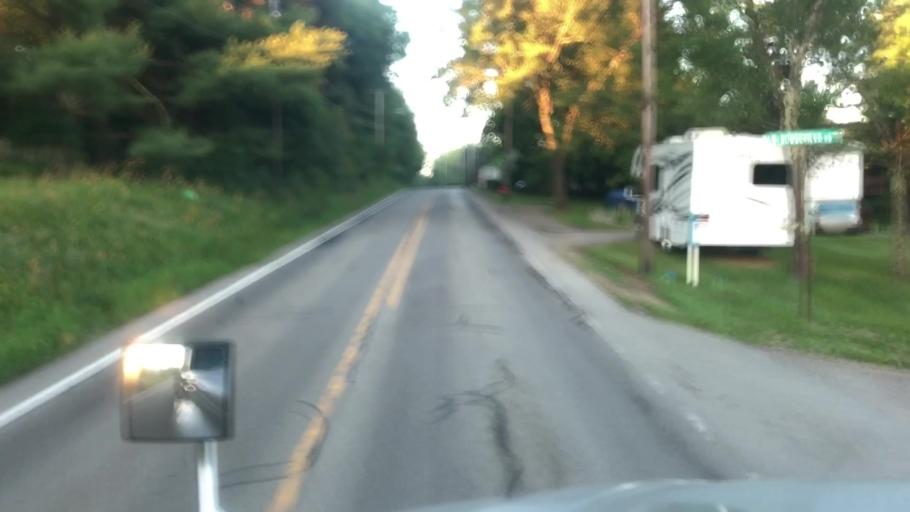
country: US
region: Pennsylvania
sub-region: Venango County
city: Hasson Heights
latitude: 41.4959
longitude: -79.6454
